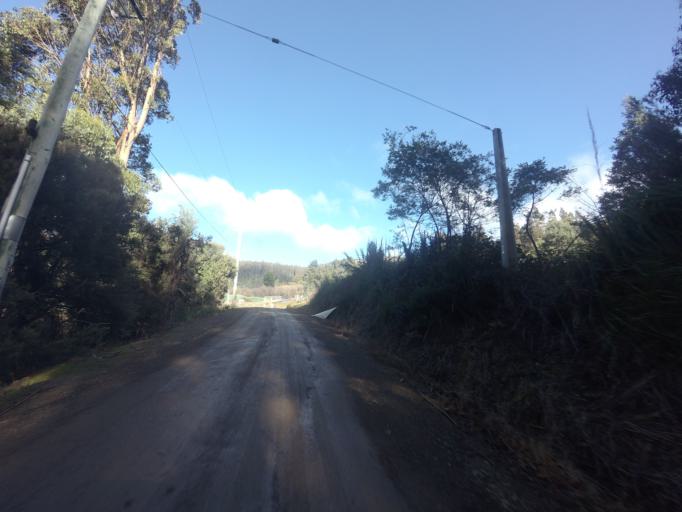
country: AU
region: Tasmania
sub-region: Glenorchy
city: Berriedale
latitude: -42.8547
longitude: 147.1672
